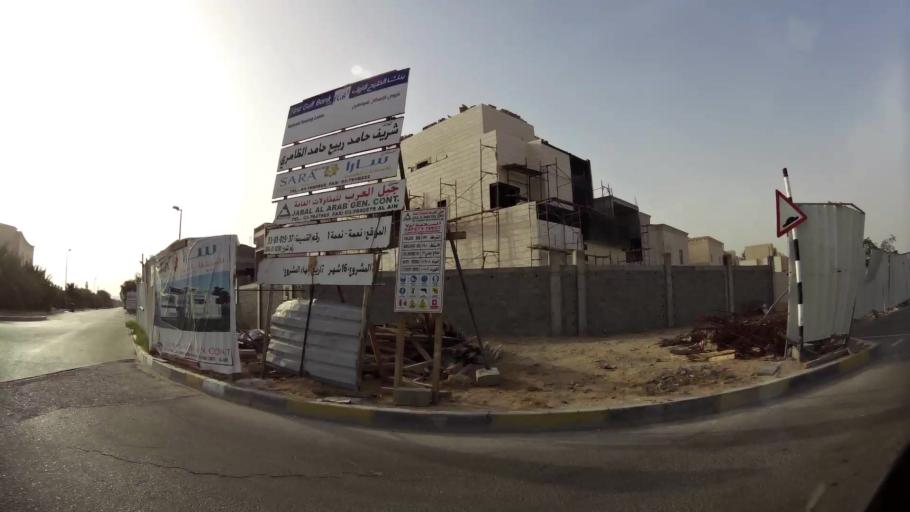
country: AE
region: Abu Dhabi
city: Al Ain
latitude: 24.1209
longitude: 55.7057
